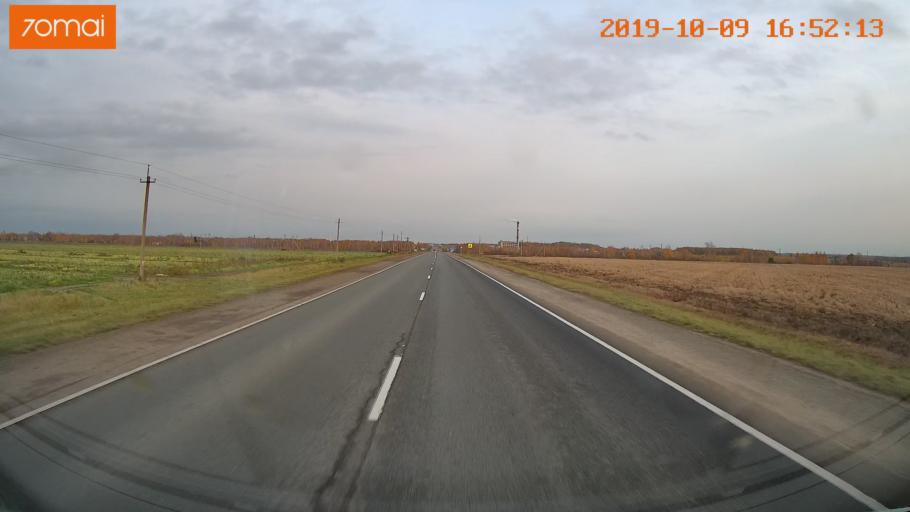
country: RU
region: Ivanovo
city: Privolzhsk
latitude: 57.3819
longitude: 41.2410
